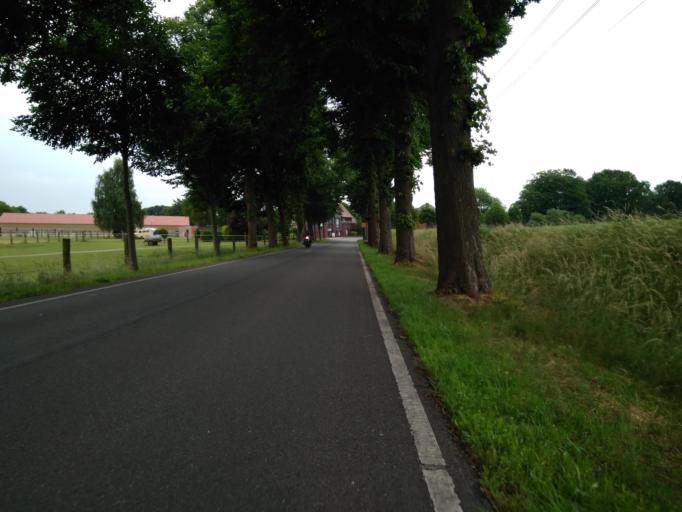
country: DE
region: North Rhine-Westphalia
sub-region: Regierungsbezirk Dusseldorf
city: Schermbeck
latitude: 51.6690
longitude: 6.8679
